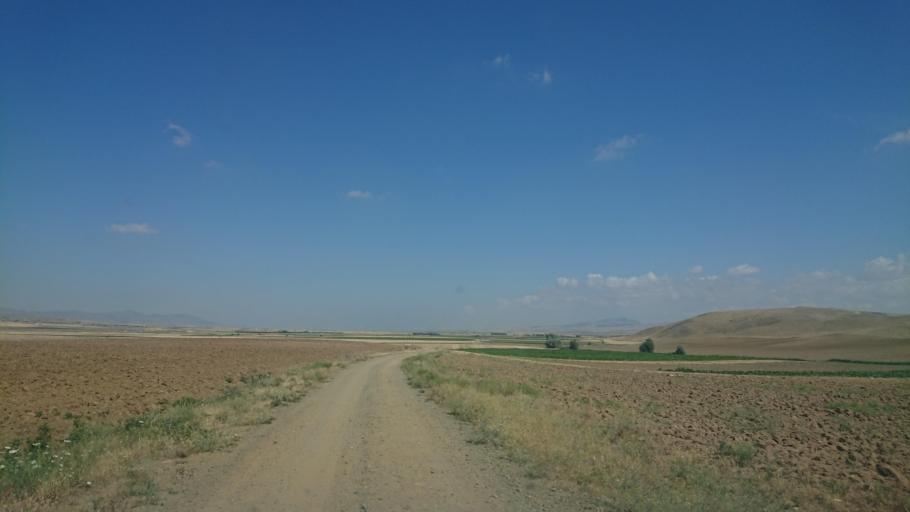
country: TR
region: Aksaray
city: Sariyahsi
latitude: 38.9681
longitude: 33.9211
